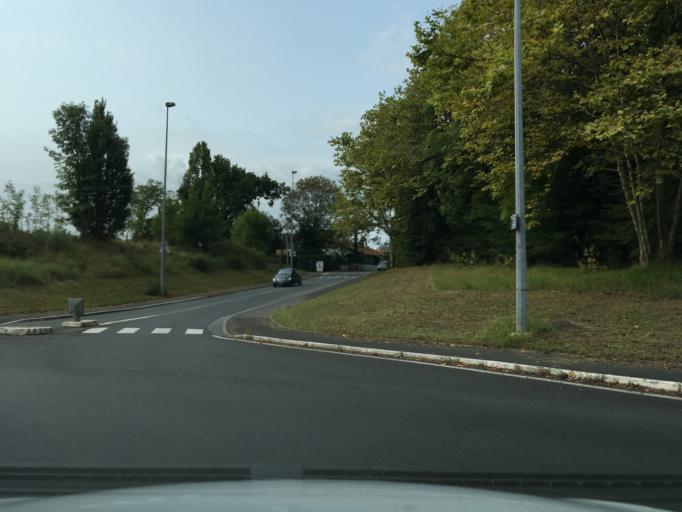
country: FR
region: Aquitaine
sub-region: Departement des Pyrenees-Atlantiques
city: Bayonne
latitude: 43.4790
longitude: -1.4557
